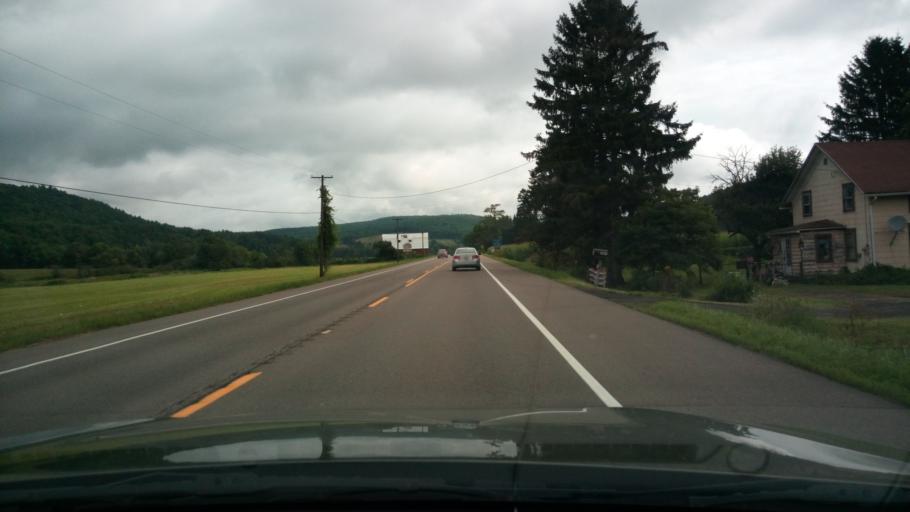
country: US
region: New York
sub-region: Schuyler County
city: Montour Falls
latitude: 42.3135
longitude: -76.6684
